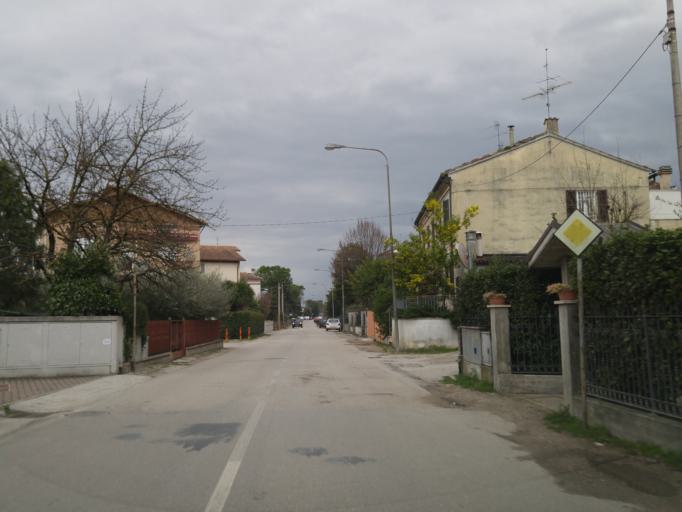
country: IT
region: The Marches
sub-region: Provincia di Pesaro e Urbino
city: Centinarola
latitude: 43.8312
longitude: 12.9896
